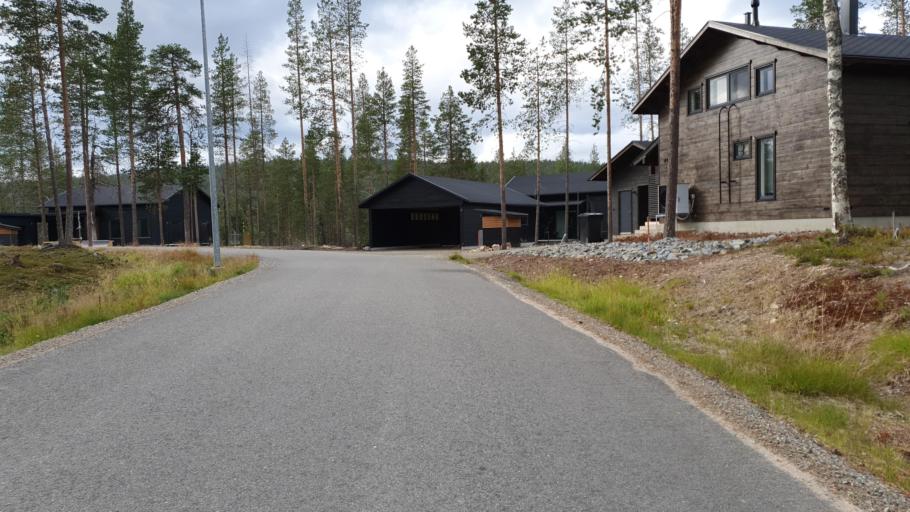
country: FI
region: Lapland
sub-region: Tunturi-Lappi
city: Kolari
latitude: 67.5950
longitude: 24.1270
